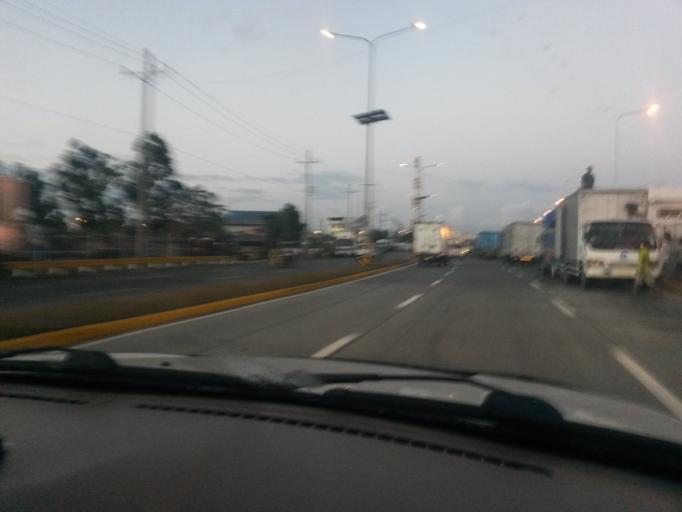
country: PH
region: Calabarzon
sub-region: Province of Batangas
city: Batangas
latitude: 13.7585
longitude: 121.0446
